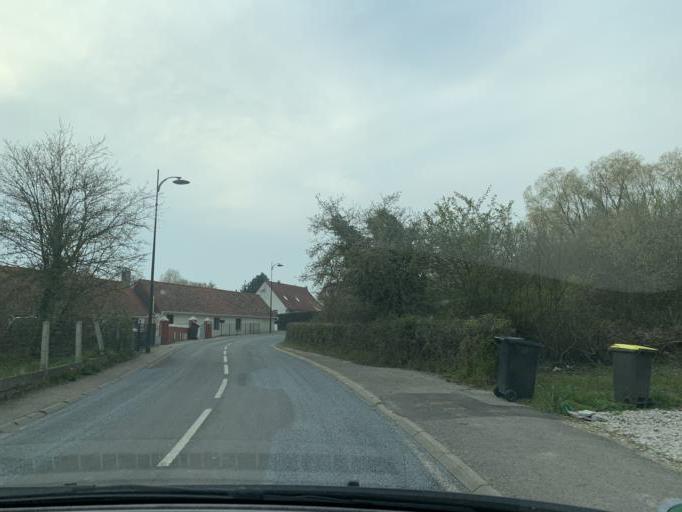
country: FR
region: Nord-Pas-de-Calais
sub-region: Departement du Pas-de-Calais
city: Longfosse
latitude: 50.7003
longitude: 1.7847
